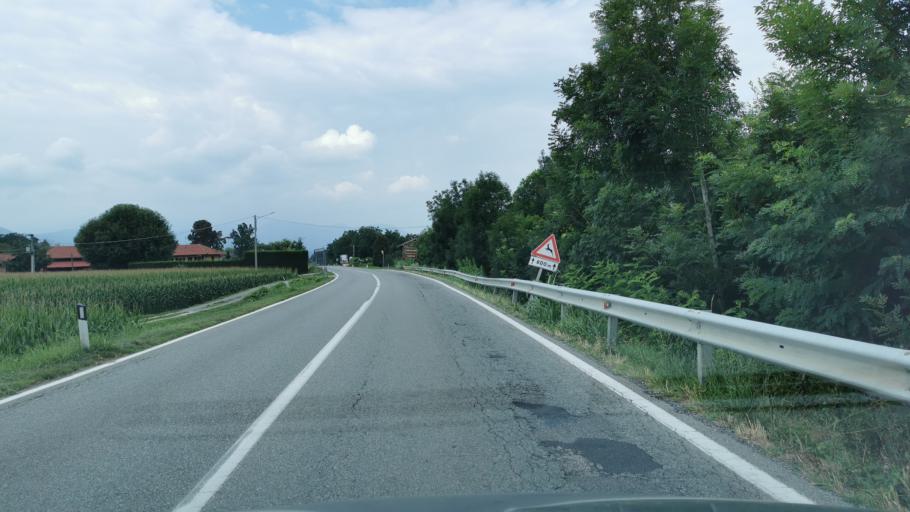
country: IT
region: Piedmont
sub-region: Provincia di Torino
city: Garzigliana
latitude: 44.8228
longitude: 7.3703
